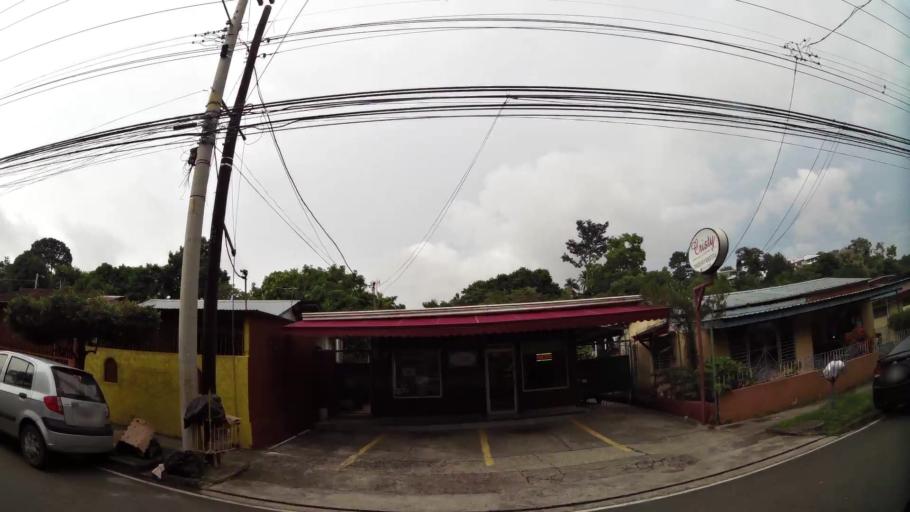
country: PA
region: Panama
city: Panama
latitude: 9.0111
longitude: -79.5279
